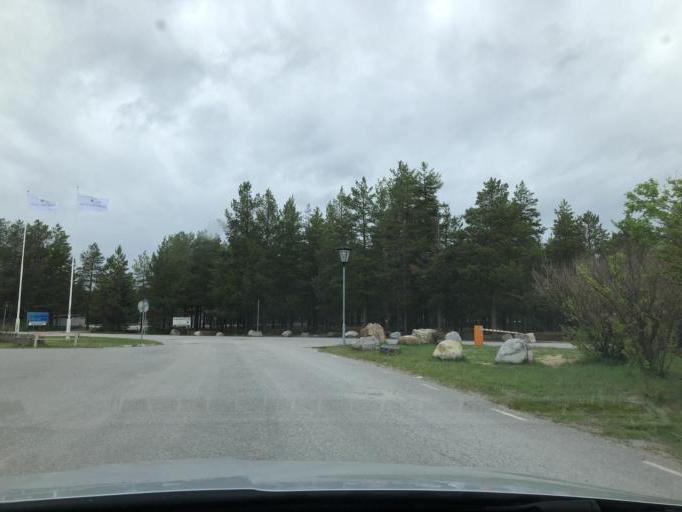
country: SE
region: Norrbotten
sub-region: Pitea Kommun
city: Pitea
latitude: 65.2360
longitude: 21.5298
